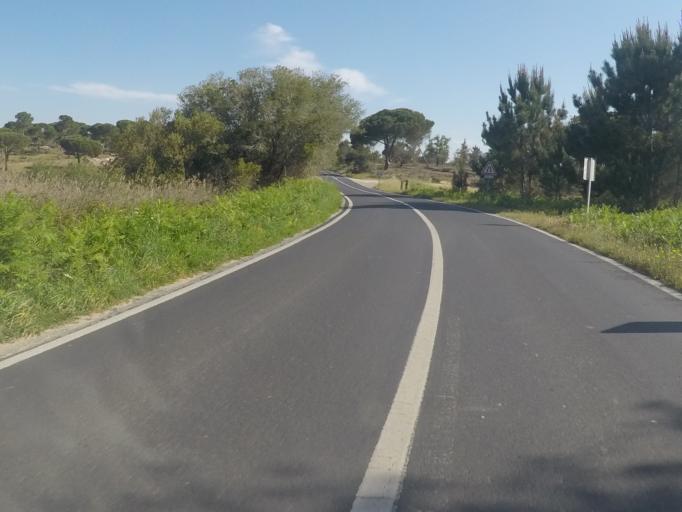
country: PT
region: Setubal
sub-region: Sesimbra
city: Sesimbra
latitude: 38.5096
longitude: -9.1453
